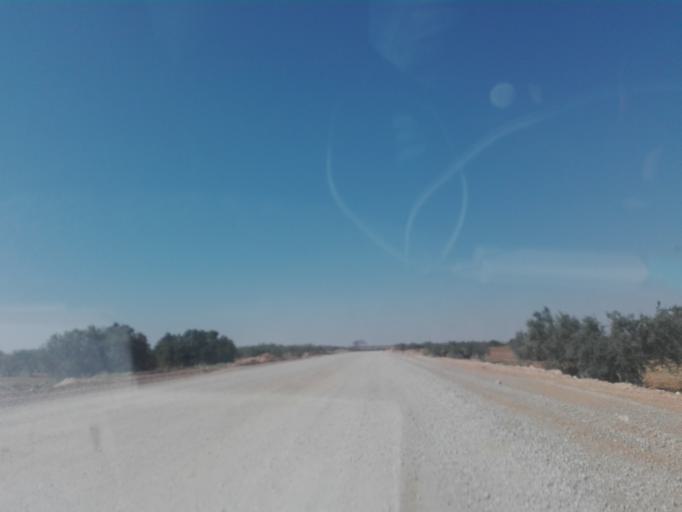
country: TN
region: Safaqis
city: Sfax
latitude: 34.7078
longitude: 10.4945
